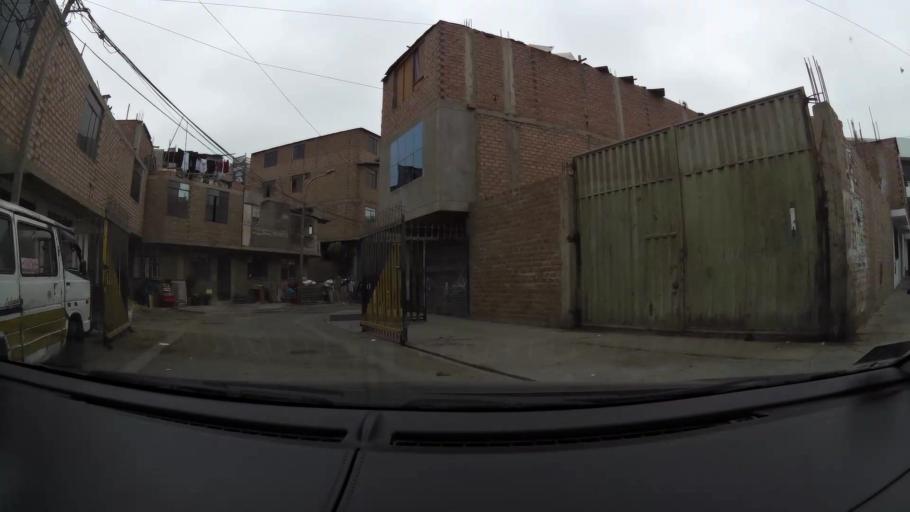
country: PE
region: Lima
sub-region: Lima
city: Independencia
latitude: -11.9532
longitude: -77.0809
